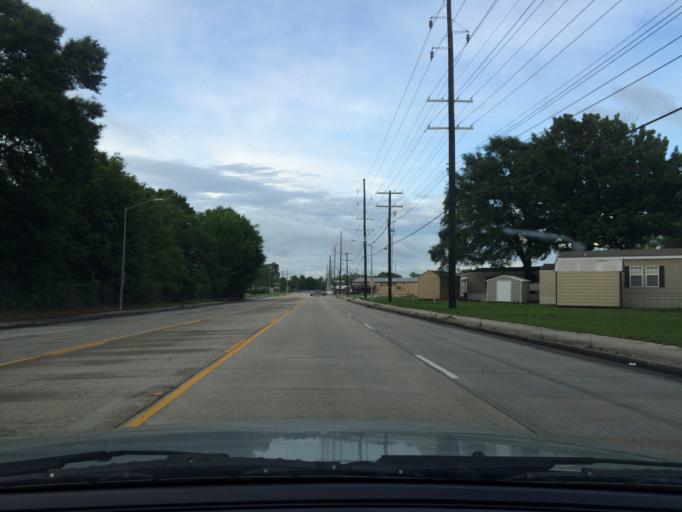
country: US
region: Louisiana
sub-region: Lafayette Parish
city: Scott
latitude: 30.2202
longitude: -92.0638
